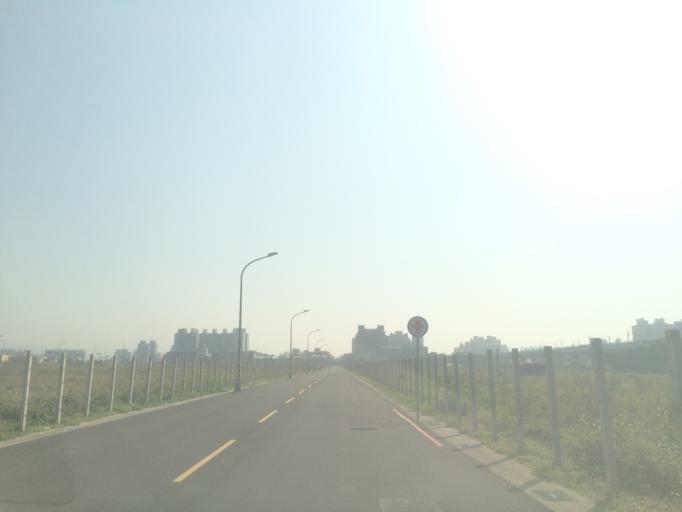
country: TW
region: Taiwan
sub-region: Taichung City
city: Taichung
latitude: 24.1781
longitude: 120.7029
